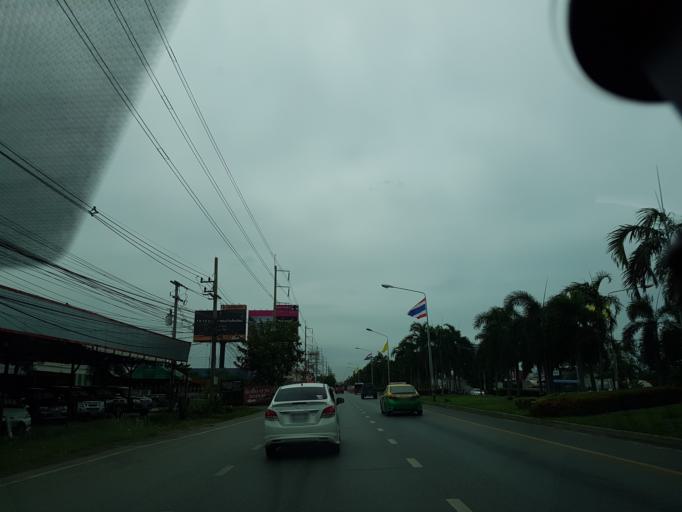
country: TH
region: Phra Nakhon Si Ayutthaya
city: Ban Bang Kadi Pathum Thani
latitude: 13.9986
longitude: 100.5725
